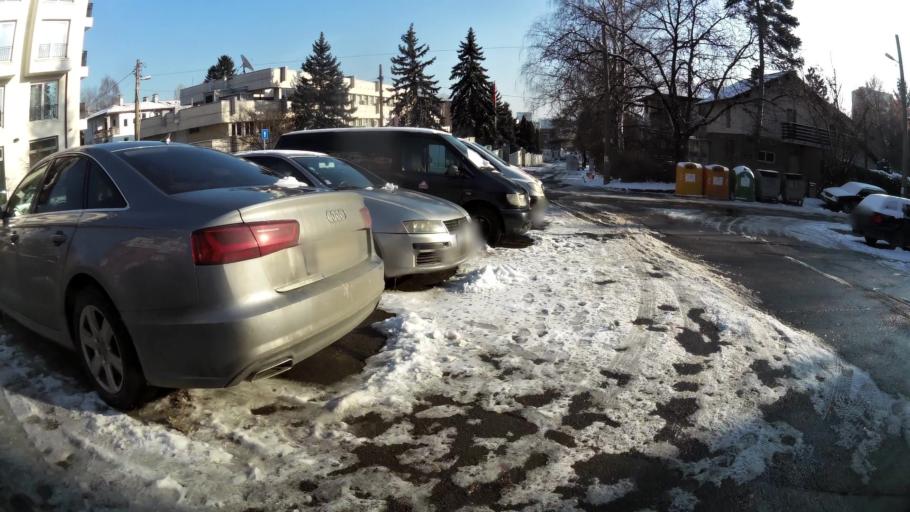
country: BG
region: Sofia-Capital
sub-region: Stolichna Obshtina
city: Sofia
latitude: 42.6709
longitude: 23.3479
